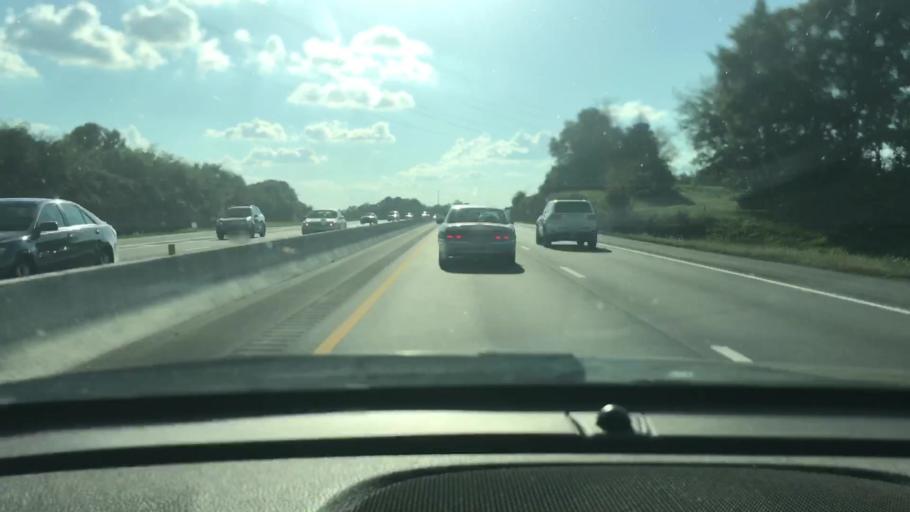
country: US
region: Tennessee
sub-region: Sumner County
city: Hendersonville
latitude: 36.3152
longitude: -86.6517
